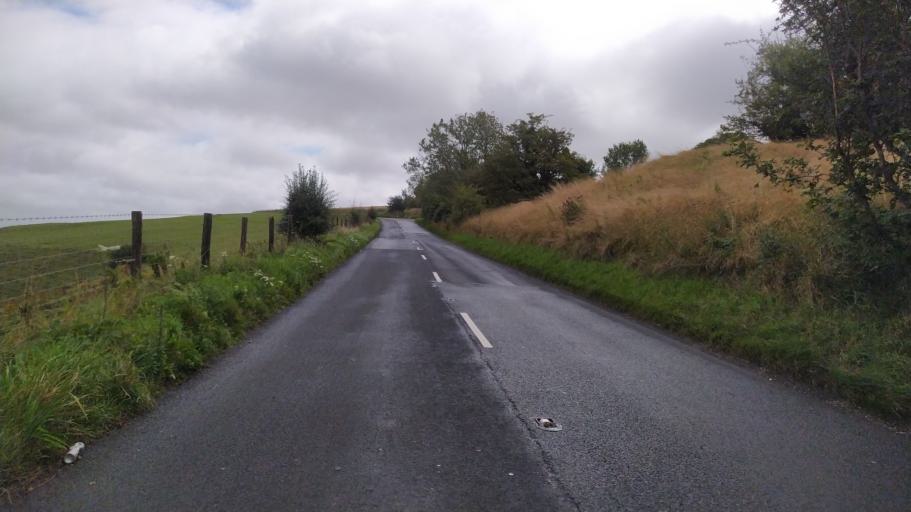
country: GB
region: England
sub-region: Dorset
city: Shaftesbury
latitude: 50.9864
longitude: -2.1477
